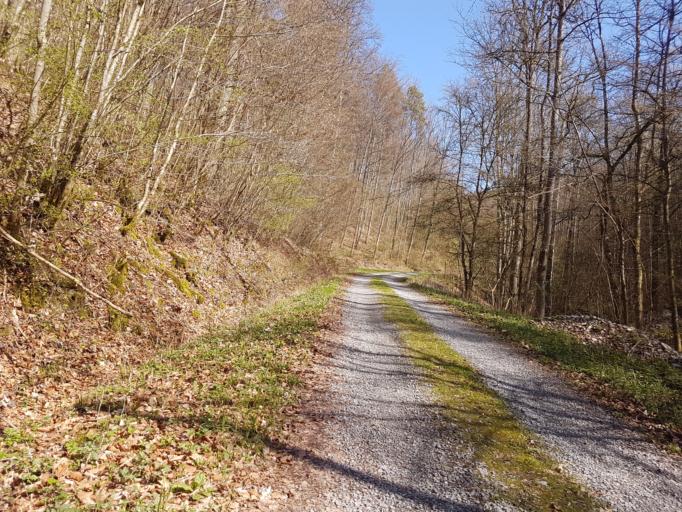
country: DE
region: Baden-Wuerttemberg
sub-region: Regierungsbezirk Stuttgart
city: Jagsthausen
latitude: 49.3358
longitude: 9.4895
